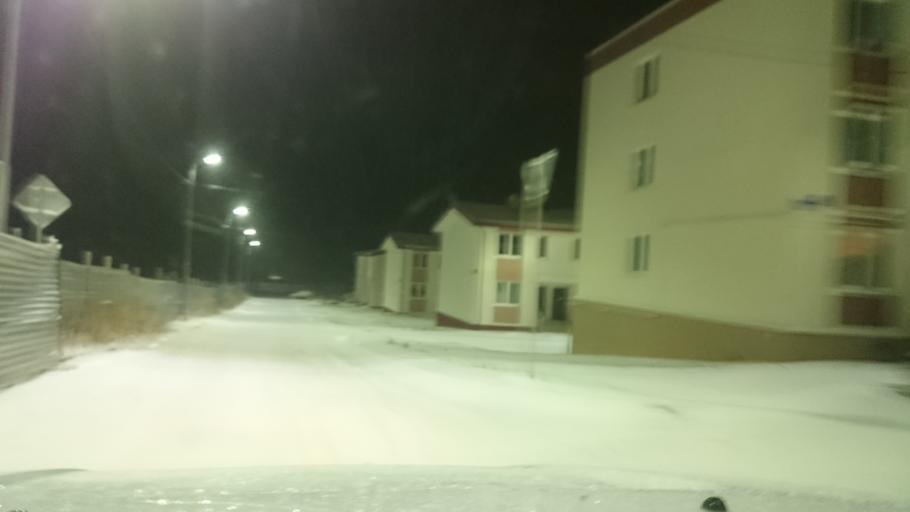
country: RU
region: Tula
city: Barsuki
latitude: 54.1933
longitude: 37.5162
